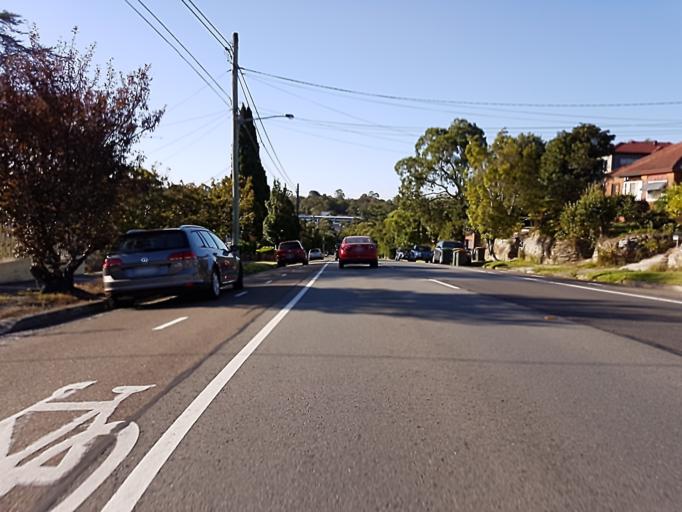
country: AU
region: New South Wales
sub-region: Ku-ring-gai
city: Roseville Chase
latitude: -33.7891
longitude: 151.1975
